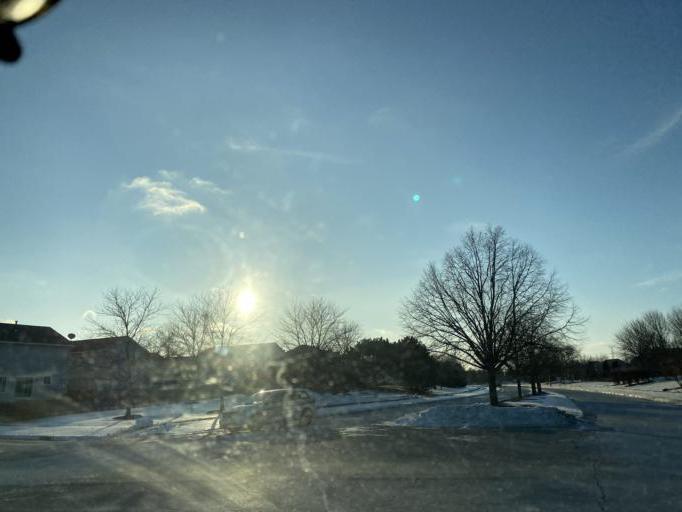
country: US
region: Illinois
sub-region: Will County
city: Romeoville
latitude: 41.6280
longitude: -88.1255
